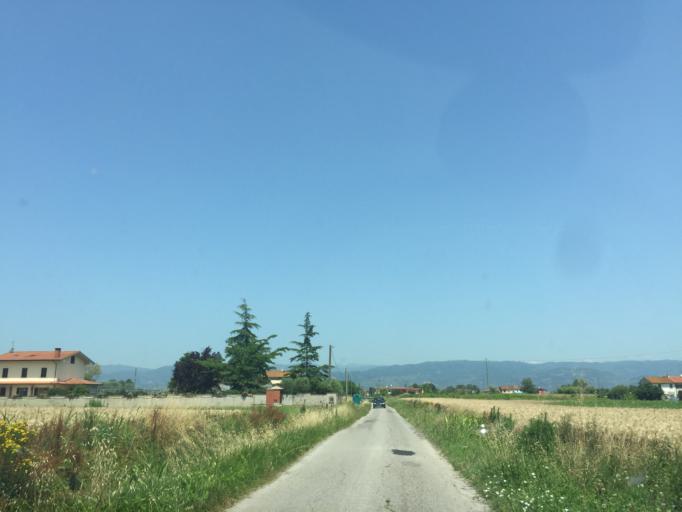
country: IT
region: Tuscany
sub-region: Provincia di Pistoia
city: Anchione
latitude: 43.8220
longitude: 10.7657
